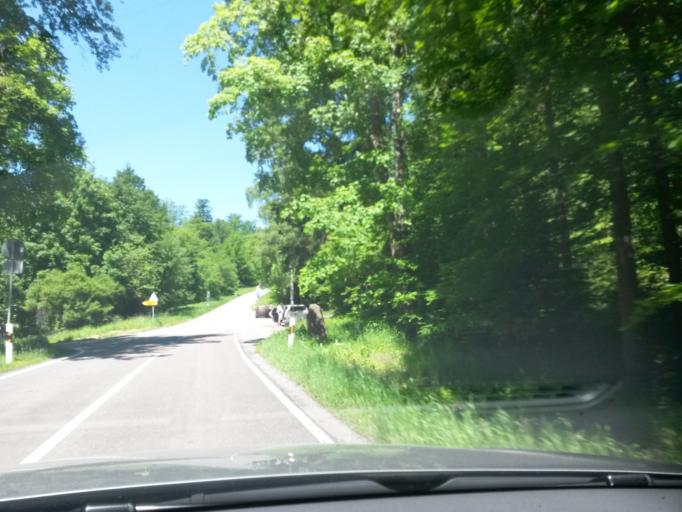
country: DE
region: Baden-Wuerttemberg
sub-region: Karlsruhe Region
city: Tiefenbronn
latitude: 48.8520
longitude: 8.7662
